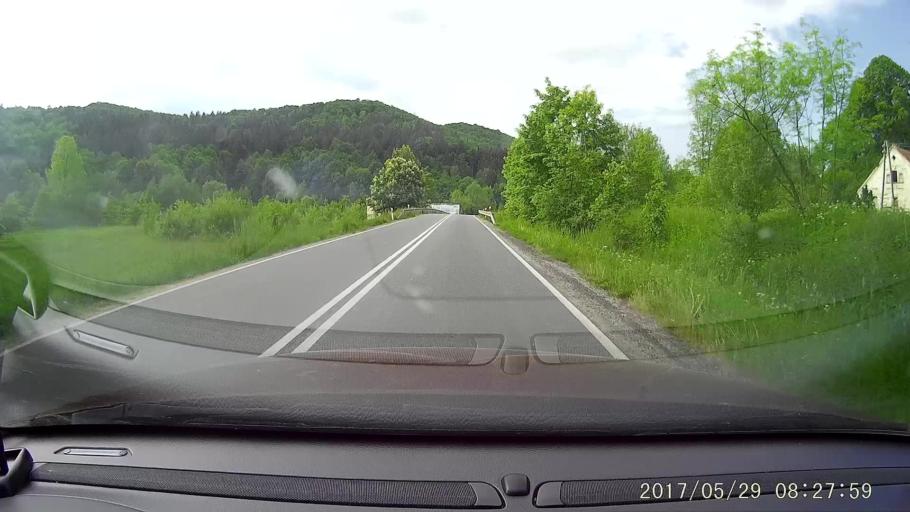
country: PL
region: Lower Silesian Voivodeship
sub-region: Powiat zlotoryjski
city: Swierzawa
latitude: 51.0430
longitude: 15.8736
